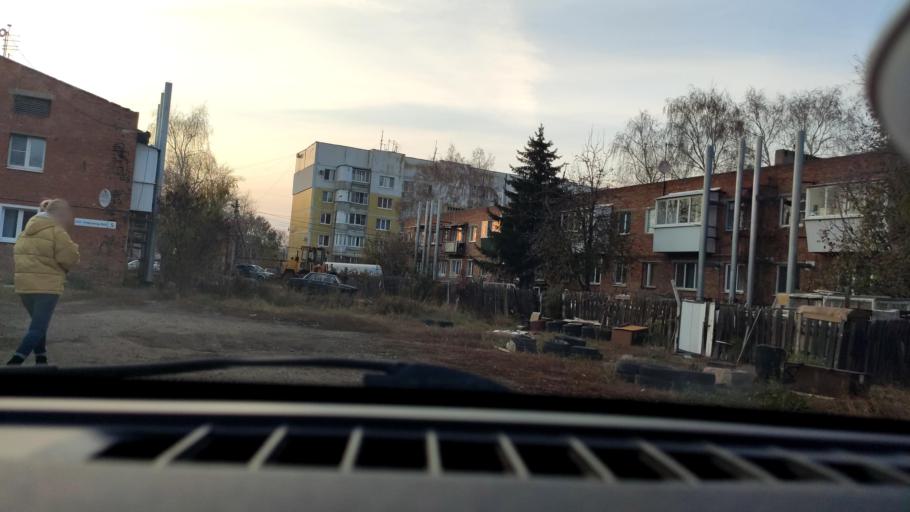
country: RU
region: Samara
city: Samara
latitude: 53.1477
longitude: 50.1396
